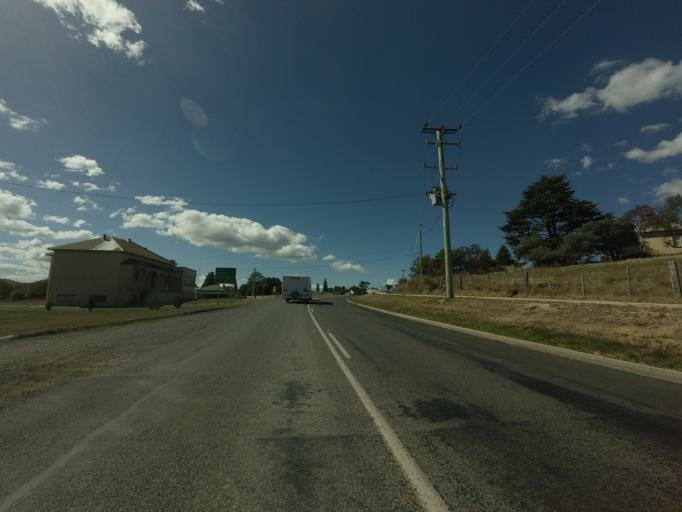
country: AU
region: Tasmania
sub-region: Break O'Day
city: St Helens
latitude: -41.6394
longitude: 147.9652
